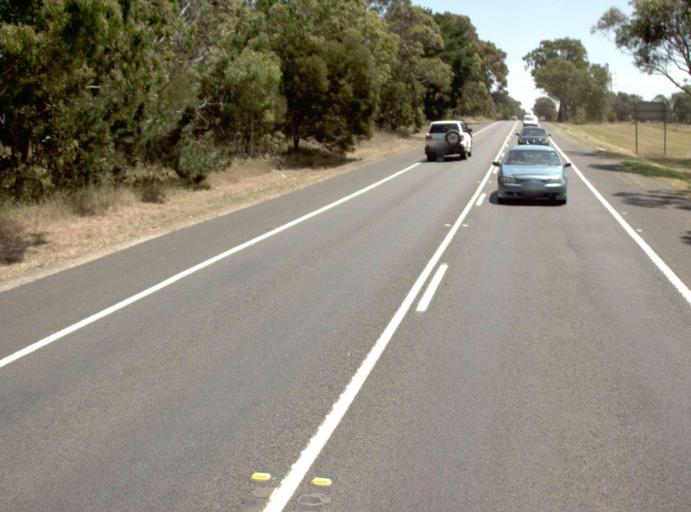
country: AU
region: Victoria
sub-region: Latrobe
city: Traralgon
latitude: -38.1826
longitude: 146.6087
